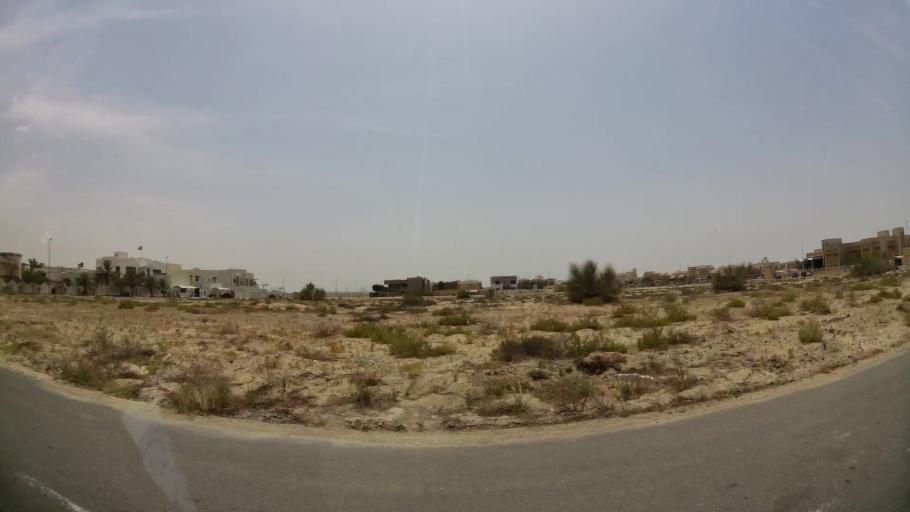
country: AE
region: Ash Shariqah
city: Sharjah
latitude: 25.2410
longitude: 55.4220
